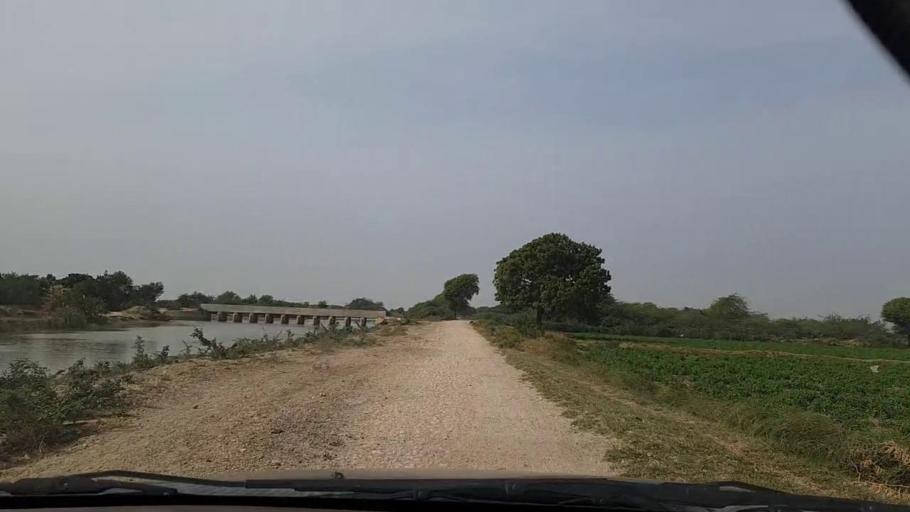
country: PK
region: Sindh
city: Thatta
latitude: 24.5727
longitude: 67.8526
